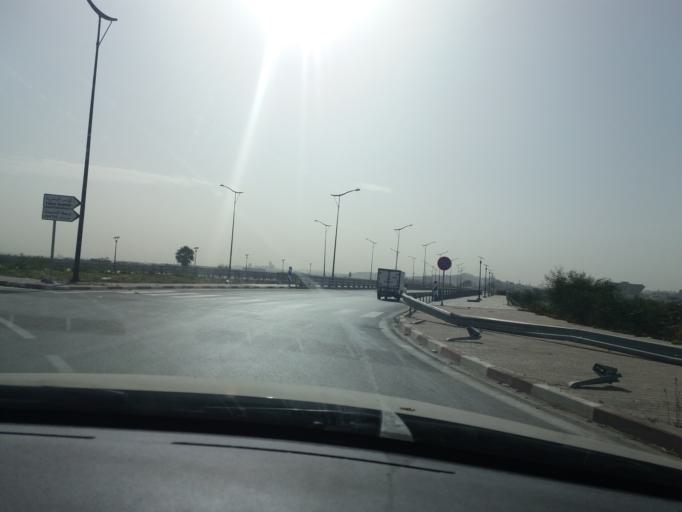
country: TN
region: Tunis
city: Tunis
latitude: 36.8130
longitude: 10.1940
